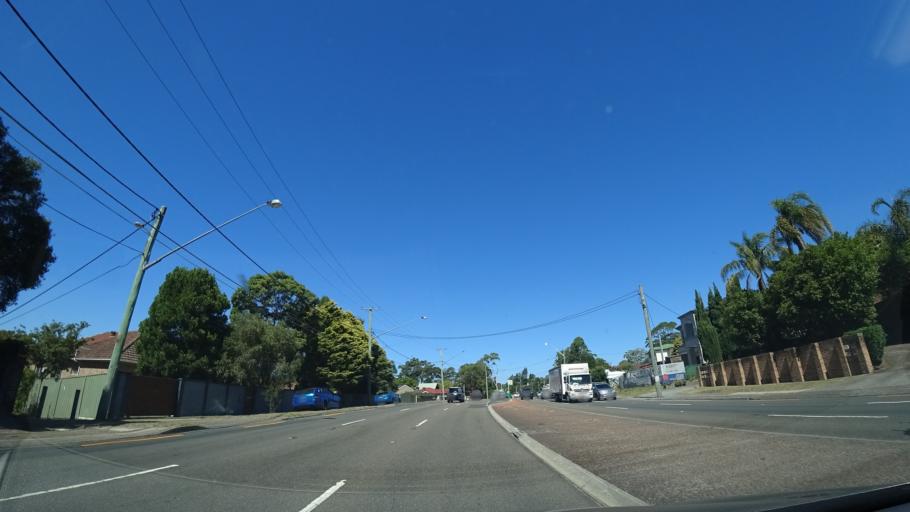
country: AU
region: New South Wales
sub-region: Warringah
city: Forestville
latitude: -33.7599
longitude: 151.2122
